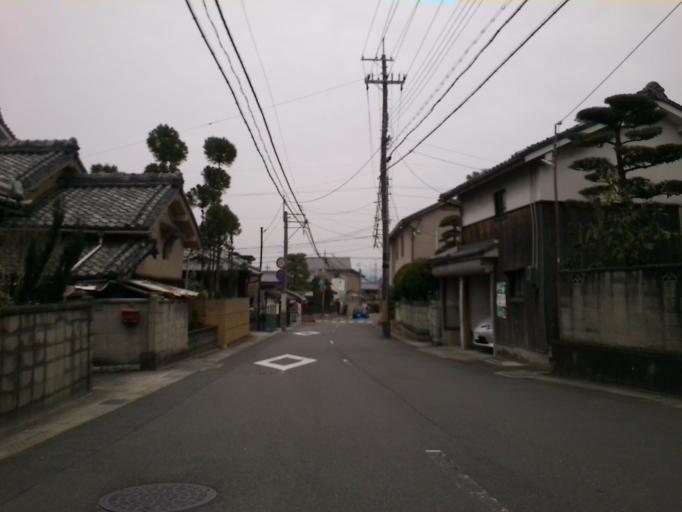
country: JP
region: Kyoto
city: Yawata
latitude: 34.8456
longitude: 135.7332
